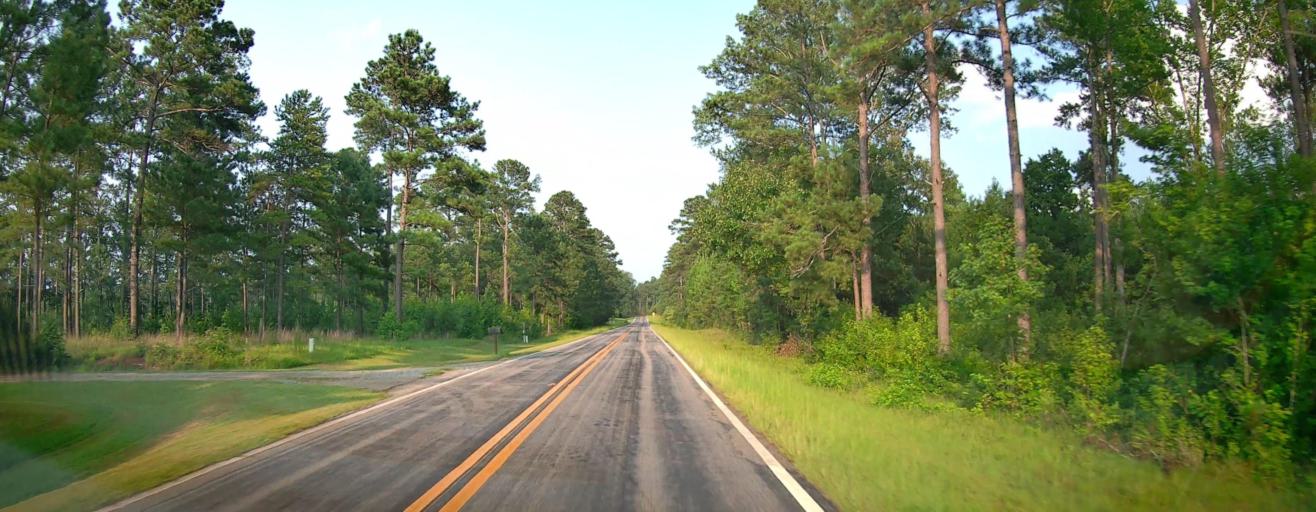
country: US
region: Georgia
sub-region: Jones County
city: Gray
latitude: 33.1124
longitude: -83.6445
